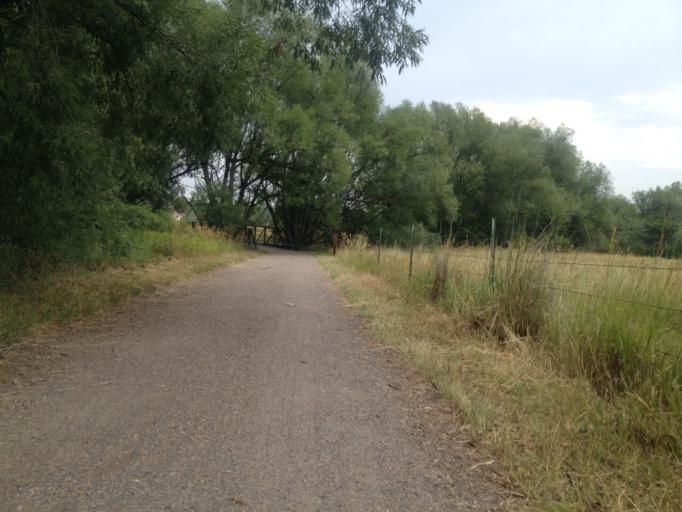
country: US
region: Colorado
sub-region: Boulder County
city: Louisville
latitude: 39.9637
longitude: -105.1406
